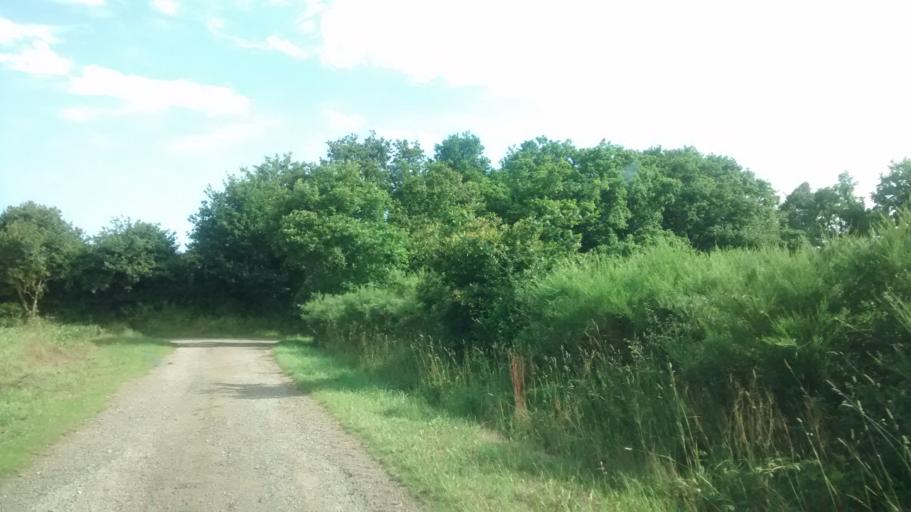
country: FR
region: Brittany
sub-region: Departement d'Ille-et-Vilaine
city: Plechatel
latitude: 47.8463
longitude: -1.7413
